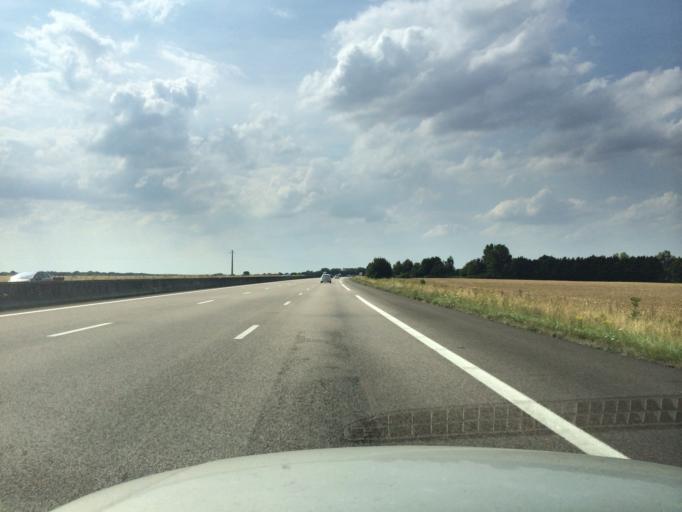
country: FR
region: Haute-Normandie
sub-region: Departement de l'Eure
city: Vernon
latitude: 49.0265
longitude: 1.4819
